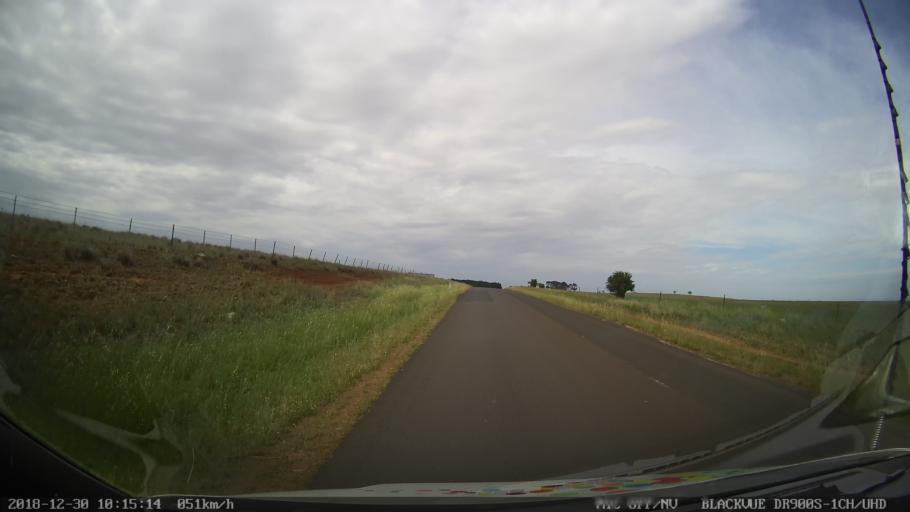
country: AU
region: New South Wales
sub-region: Snowy River
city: Berridale
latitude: -36.5422
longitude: 149.0471
